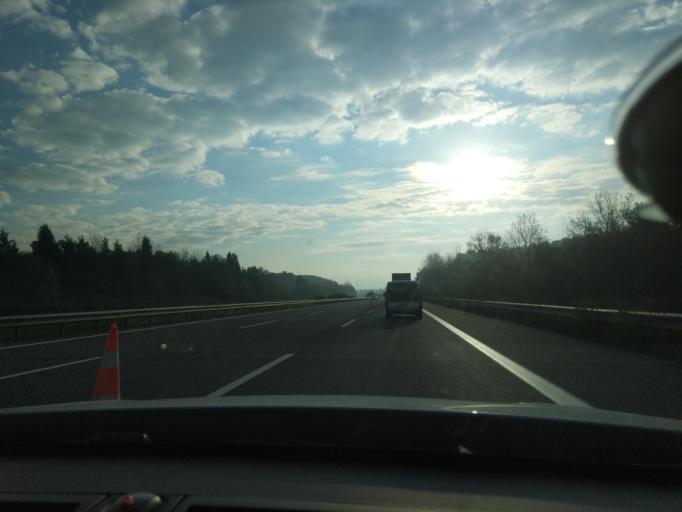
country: TR
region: Duzce
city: Duzce
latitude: 40.8113
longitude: 31.1174
